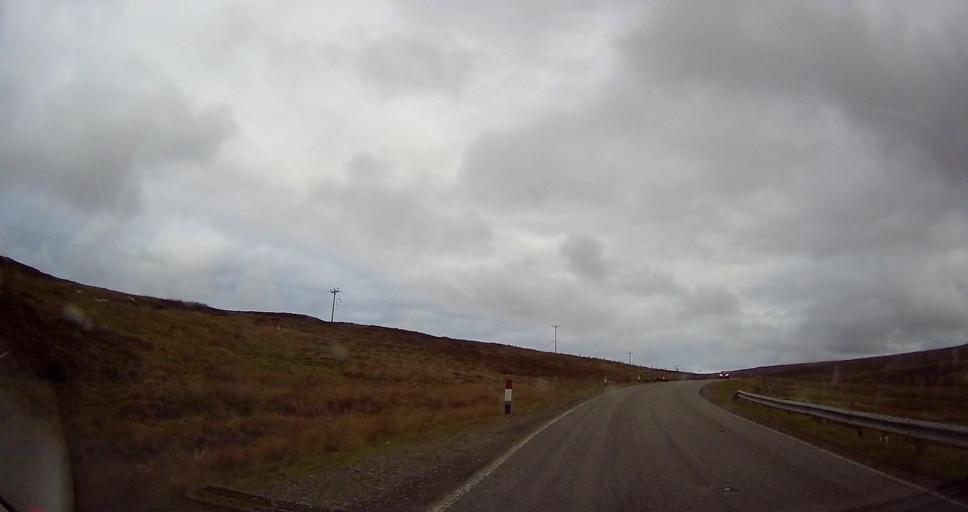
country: GB
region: Scotland
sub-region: Shetland Islands
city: Shetland
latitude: 60.6135
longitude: -1.0744
